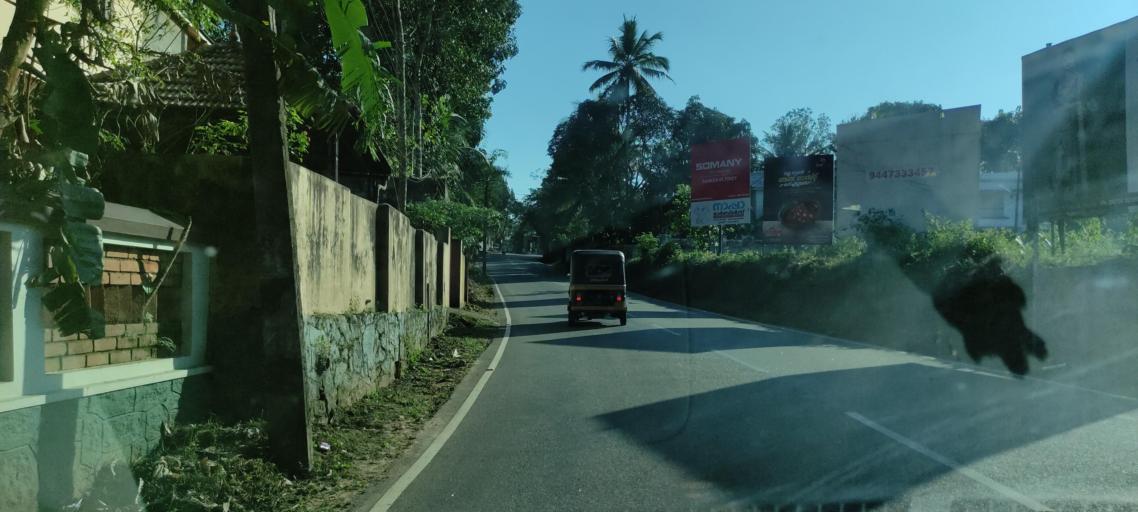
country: IN
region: Kerala
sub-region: Pattanamtitta
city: Adur
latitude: 9.1586
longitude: 76.7428
